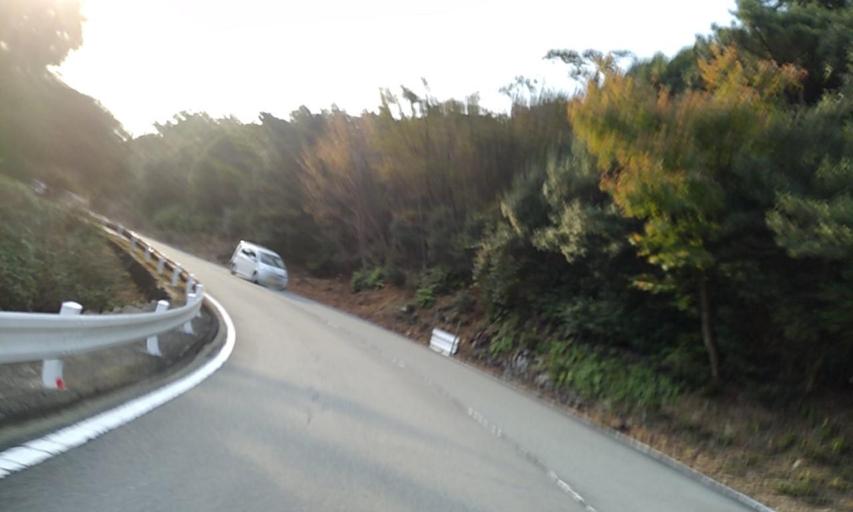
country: JP
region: Mie
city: Toba
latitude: 34.4594
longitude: 136.7715
